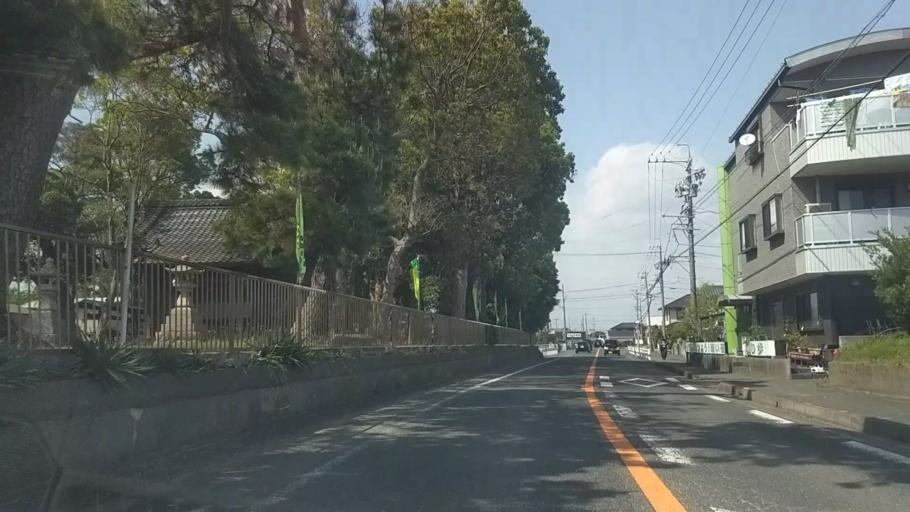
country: JP
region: Shizuoka
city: Hamamatsu
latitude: 34.6773
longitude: 137.7077
